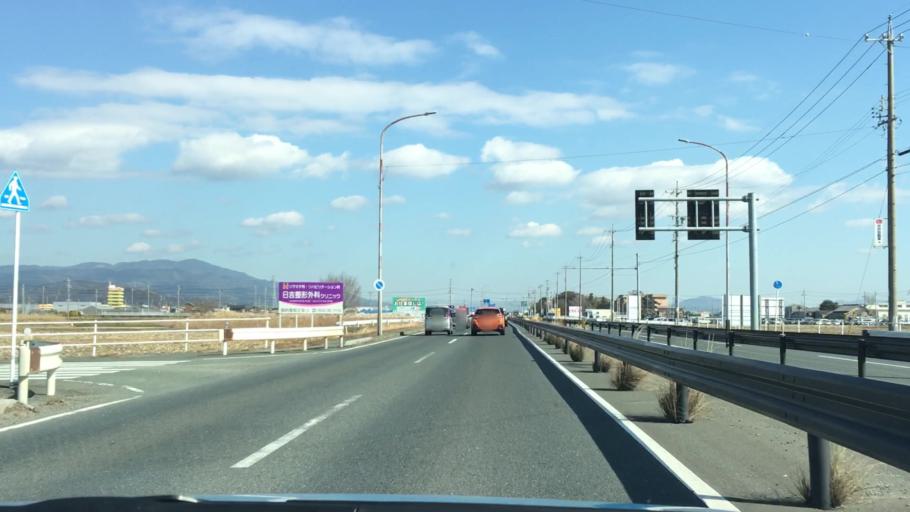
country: JP
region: Aichi
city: Kozakai-cho
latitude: 34.8202
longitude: 137.3275
